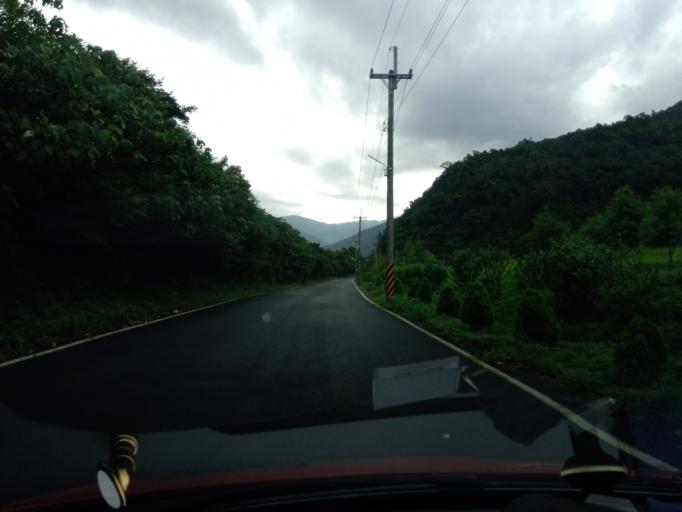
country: TW
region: Taiwan
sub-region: Yilan
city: Yilan
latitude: 24.7812
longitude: 121.7090
